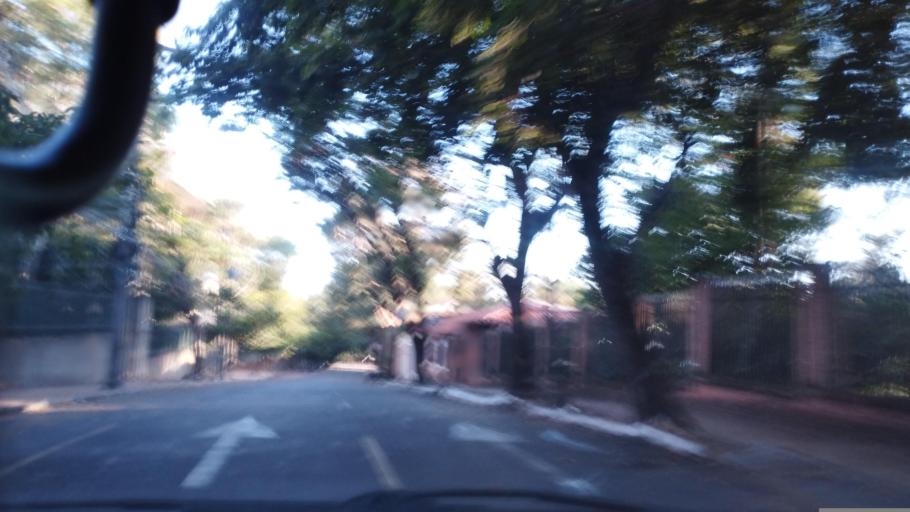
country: PY
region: Asuncion
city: Asuncion
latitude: -25.2889
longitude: -57.6114
